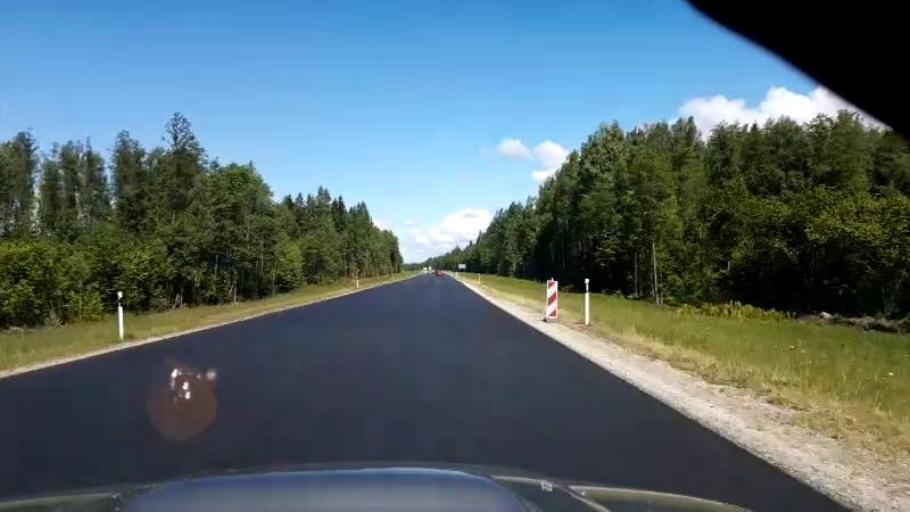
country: LV
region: Salacgrivas
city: Ainazi
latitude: 58.0366
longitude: 24.5069
